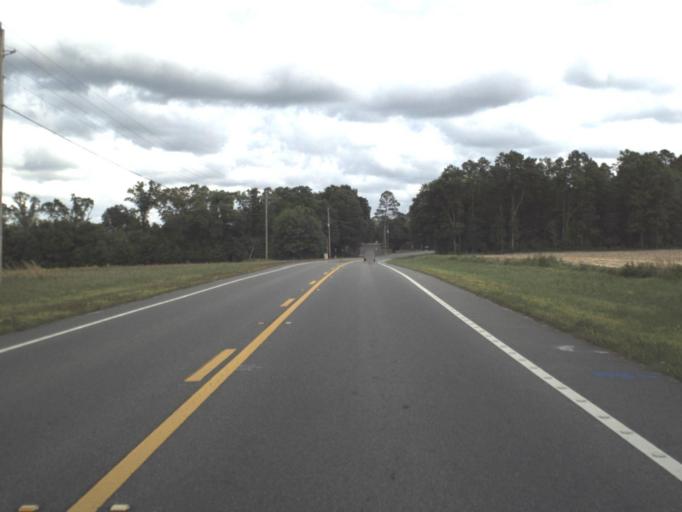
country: US
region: Alabama
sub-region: Escambia County
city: East Brewton
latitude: 30.9380
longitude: -87.0258
